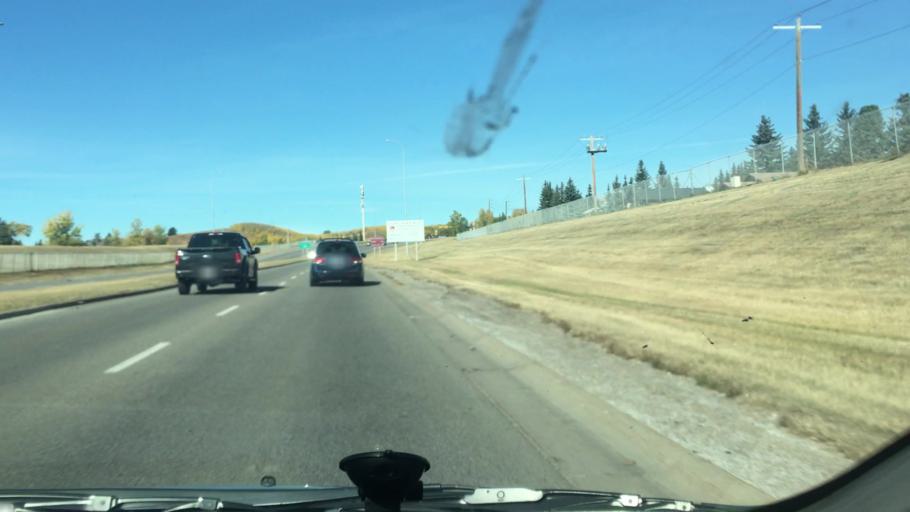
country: CA
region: Alberta
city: Calgary
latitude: 51.1182
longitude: -114.1614
